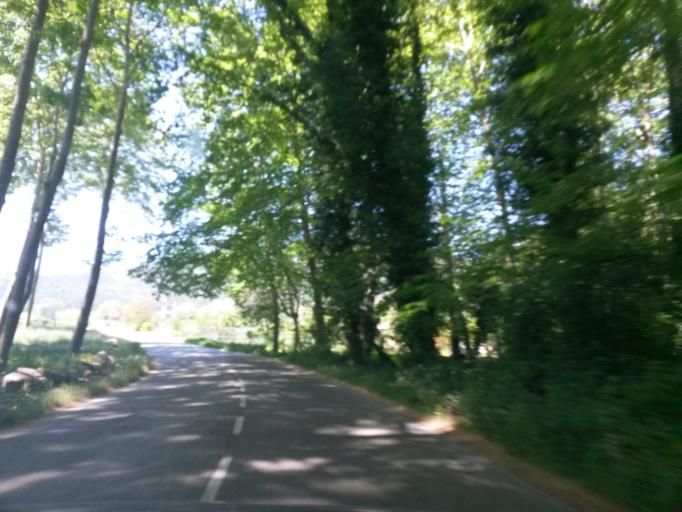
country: ES
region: Catalonia
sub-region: Provincia de Girona
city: Angles
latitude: 41.9619
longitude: 2.6337
